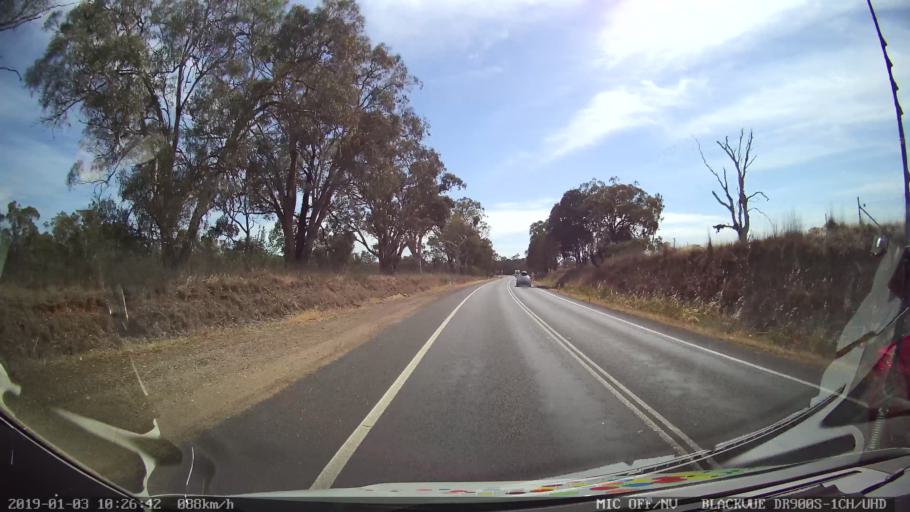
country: AU
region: New South Wales
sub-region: Young
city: Young
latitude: -34.4098
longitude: 148.2517
